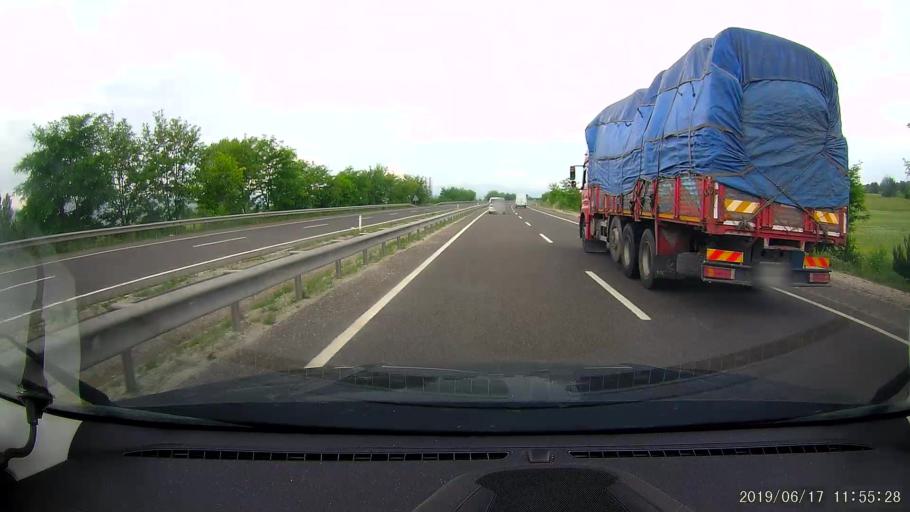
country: TR
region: Cankiri
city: Atkaracalar
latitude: 40.8006
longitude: 33.0065
